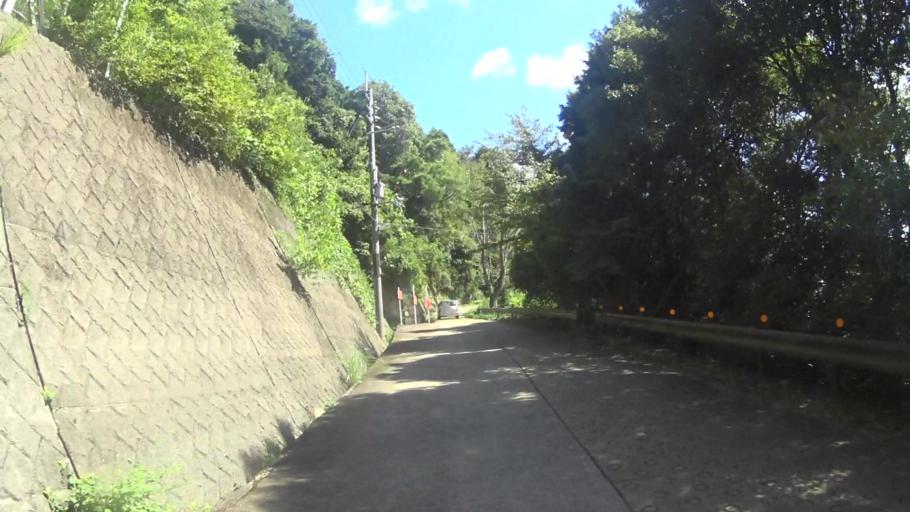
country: JP
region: Nara
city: Nara-shi
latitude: 34.7547
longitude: 135.9386
